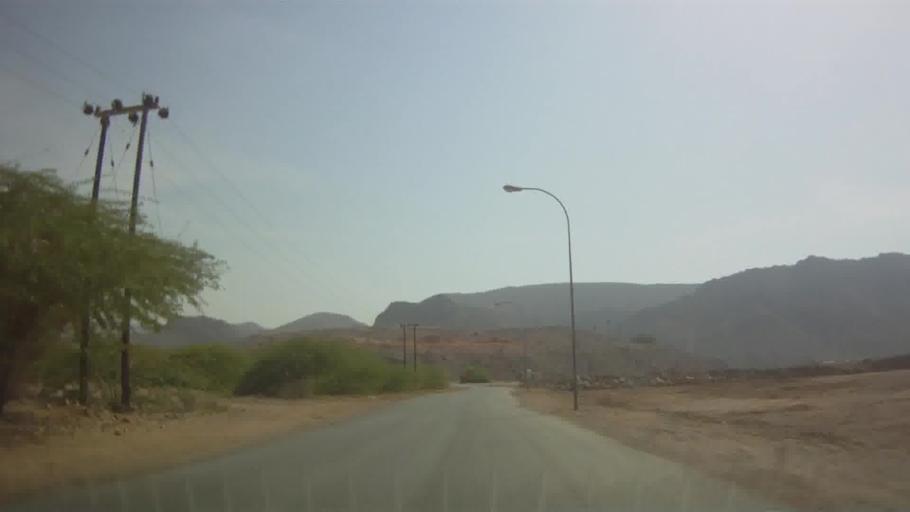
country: OM
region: Muhafazat Masqat
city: Muscat
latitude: 23.5107
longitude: 58.7351
